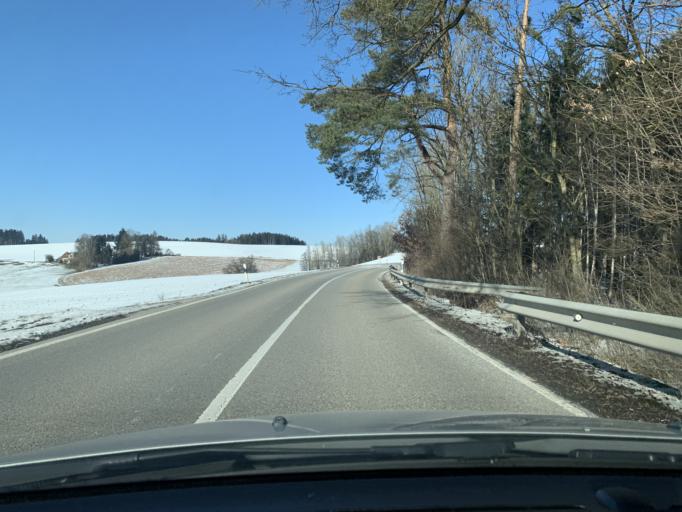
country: DE
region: Bavaria
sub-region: Upper Bavaria
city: Zangberg
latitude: 48.3030
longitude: 12.4331
